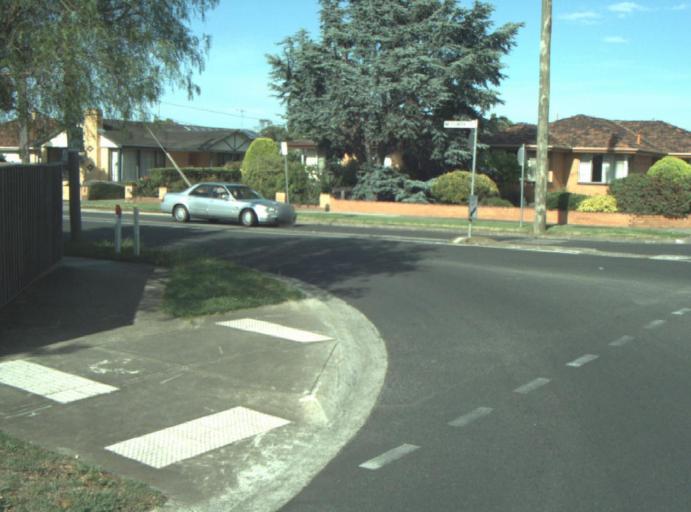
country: AU
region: Victoria
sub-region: Greater Geelong
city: Hamlyn Heights
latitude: -38.1284
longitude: 144.3204
